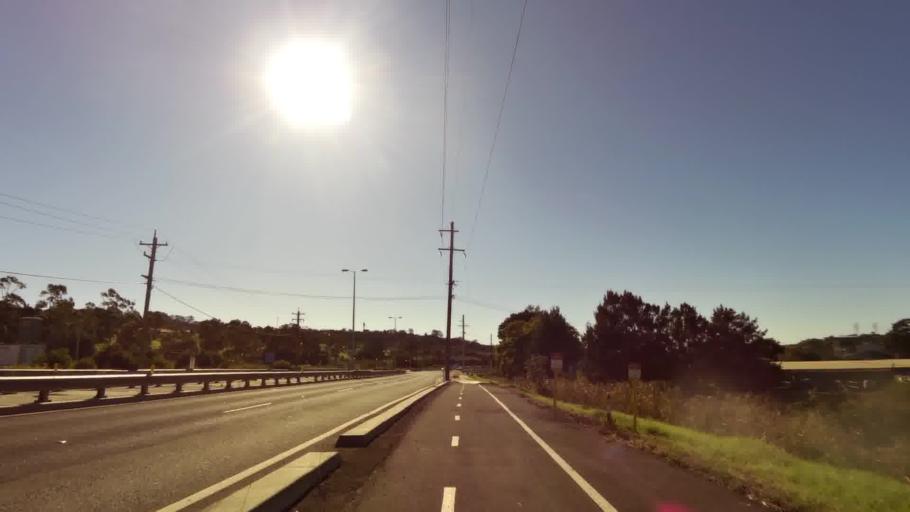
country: AU
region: New South Wales
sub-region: Wollongong
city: Koonawarra
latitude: -34.4715
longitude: 150.8170
